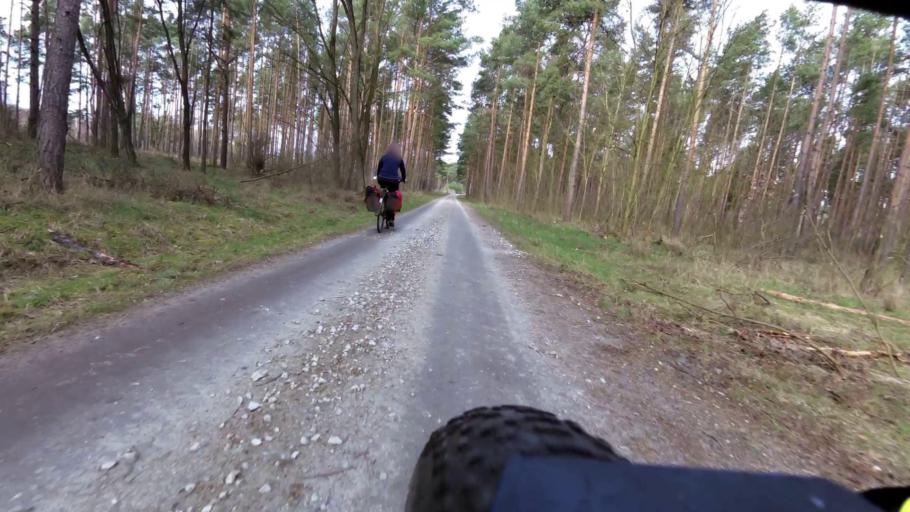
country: DE
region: Brandenburg
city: Wiesenau
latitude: 52.2845
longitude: 14.6442
